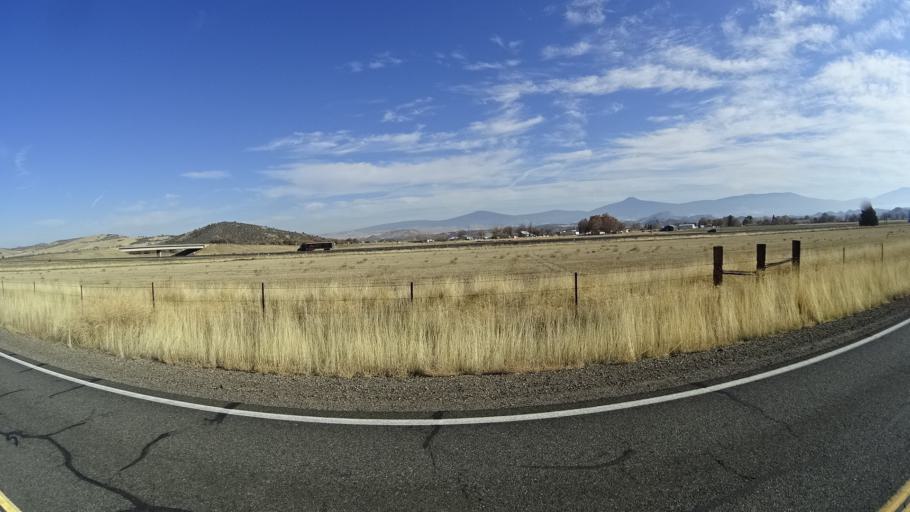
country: US
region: California
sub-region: Siskiyou County
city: Montague
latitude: 41.6436
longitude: -122.5361
